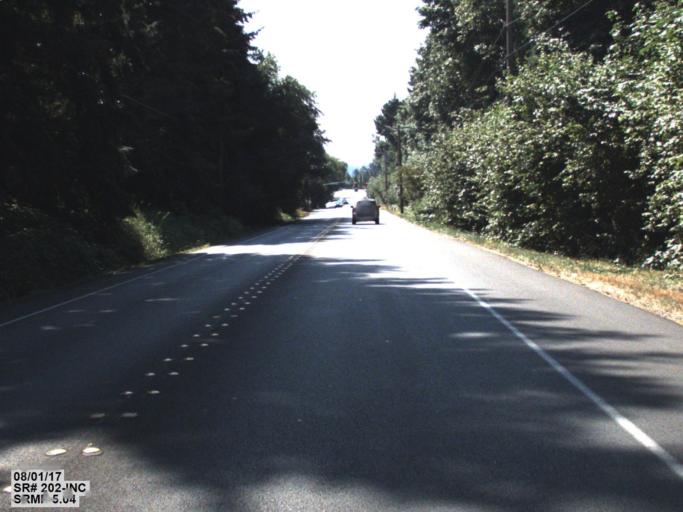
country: US
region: Washington
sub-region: King County
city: Redmond
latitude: 47.7000
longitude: -122.1321
